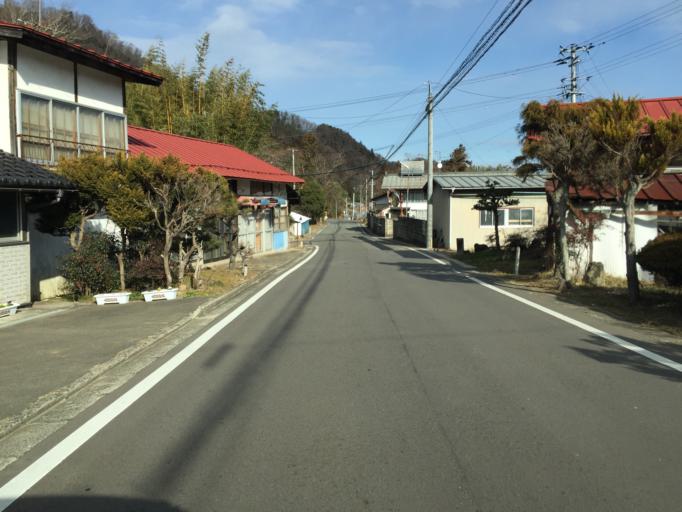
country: JP
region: Fukushima
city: Hobaramachi
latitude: 37.7489
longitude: 140.5660
